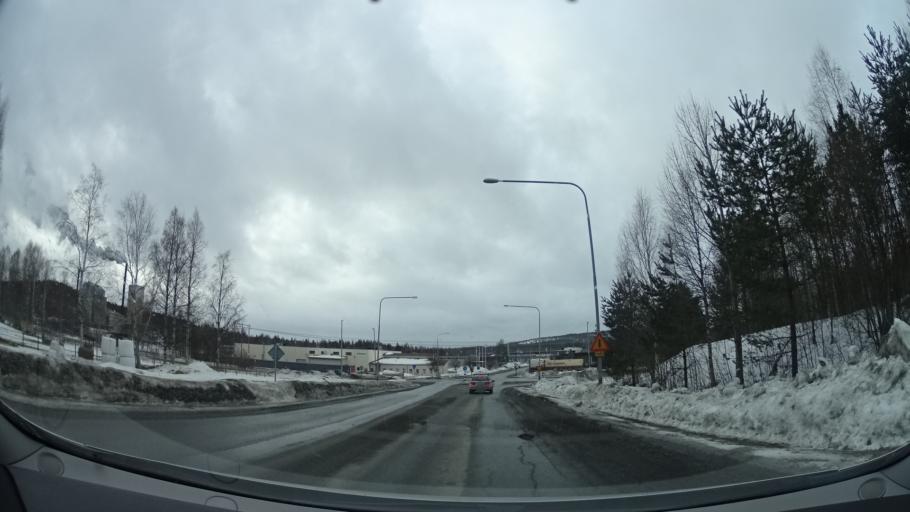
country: SE
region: Vaesterbotten
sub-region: Skelleftea Kommun
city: Soedra Bergsbyn
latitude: 64.7484
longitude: 21.0357
